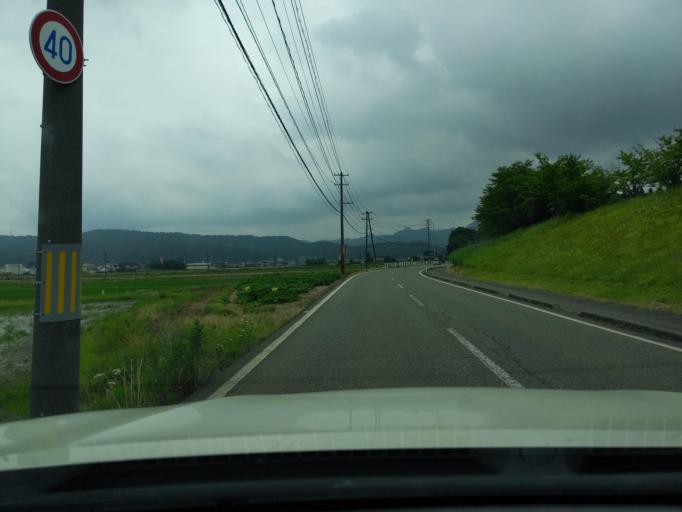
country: JP
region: Niigata
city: Kashiwazaki
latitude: 37.3473
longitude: 138.6020
